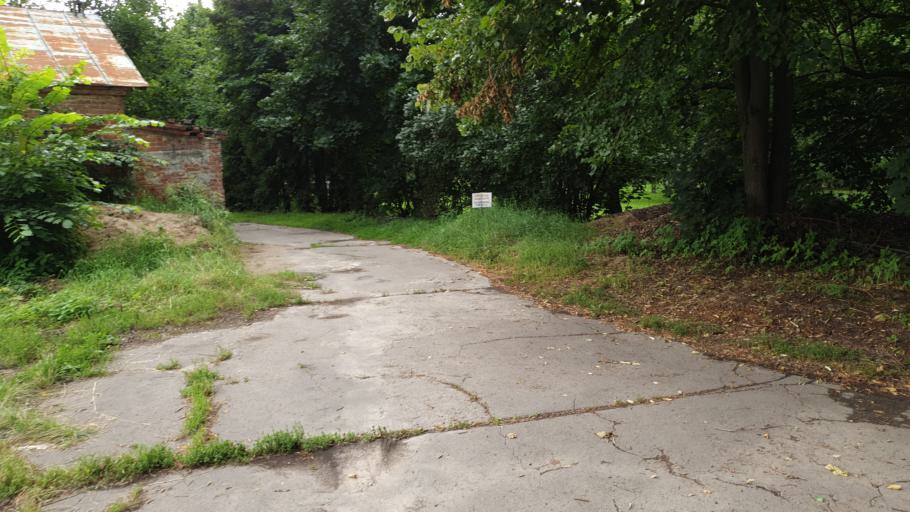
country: RU
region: Moskovskaya
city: Gorki-Leninskiye
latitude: 55.5057
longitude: 37.7669
